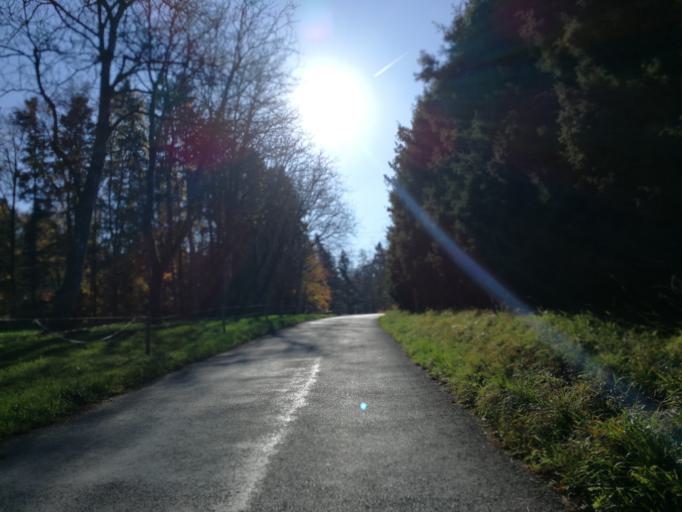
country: CH
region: Zurich
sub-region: Bezirk Uster
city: Monchaltorf
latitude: 47.3036
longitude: 8.7060
